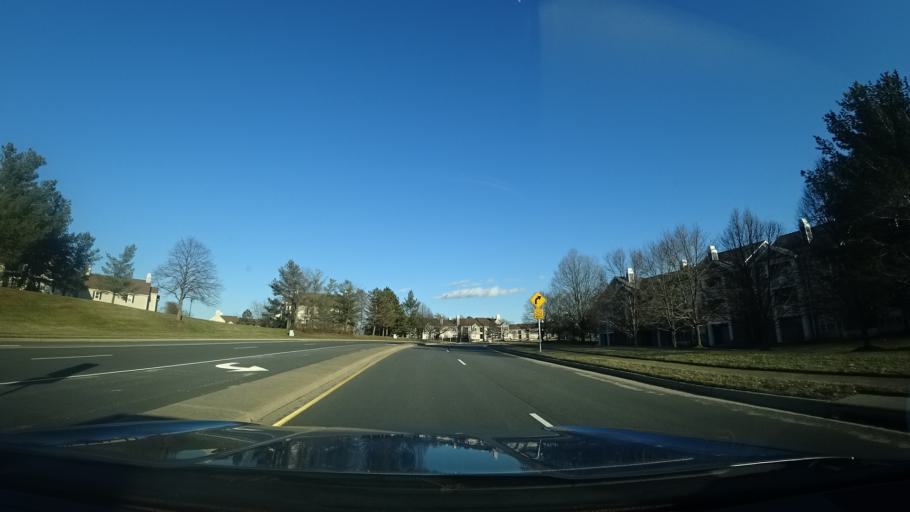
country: US
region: Virginia
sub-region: Loudoun County
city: University Center
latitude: 39.0554
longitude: -77.4396
